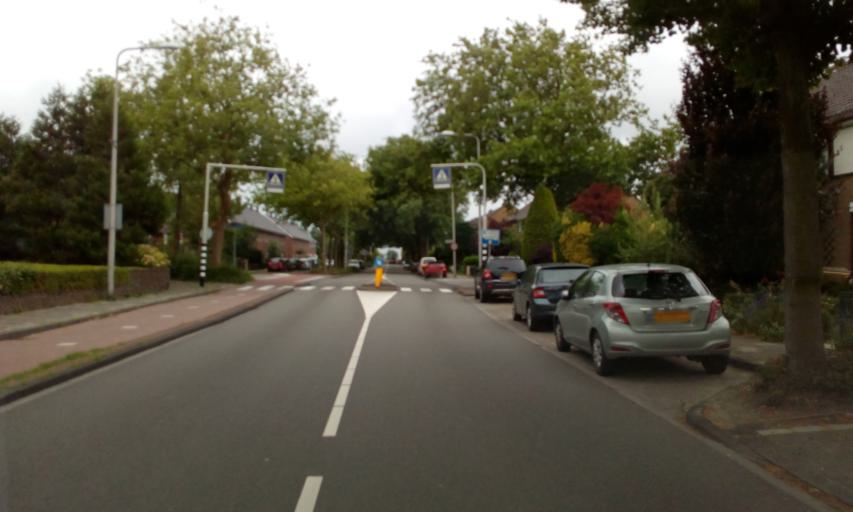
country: NL
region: South Holland
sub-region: Gemeente Westland
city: Honselersdijk
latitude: 52.0074
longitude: 4.2311
